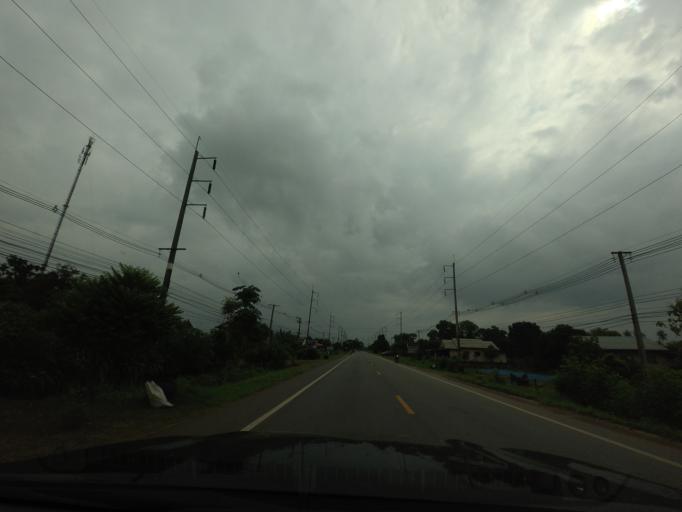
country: TH
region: Nong Khai
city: Tha Bo
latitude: 17.8918
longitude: 102.5968
